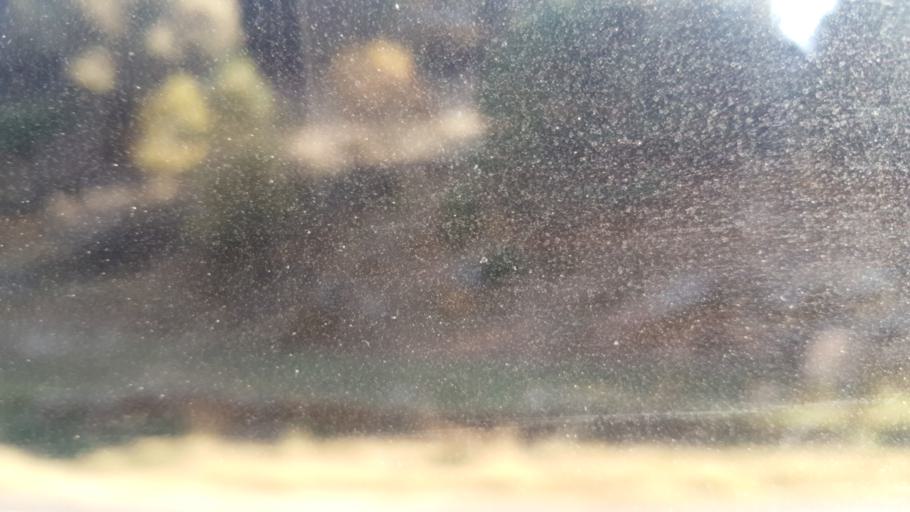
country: TR
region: Eskisehir
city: Kirka
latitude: 39.1094
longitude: 30.5853
